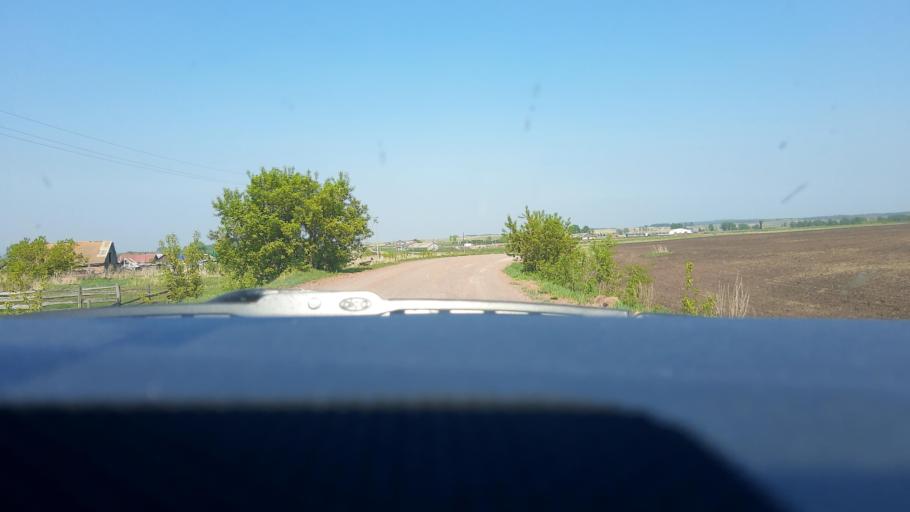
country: RU
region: Bashkortostan
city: Chishmy
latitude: 54.4399
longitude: 55.3091
